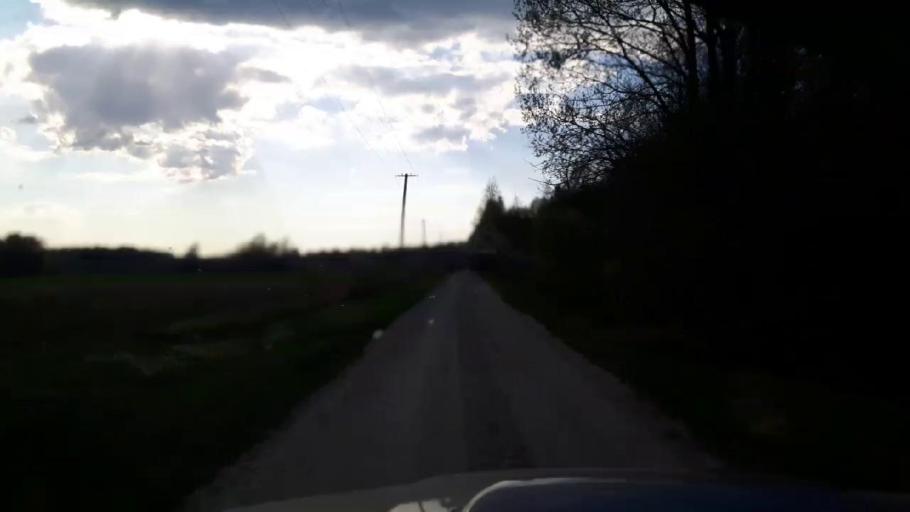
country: EE
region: Paernumaa
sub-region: Tootsi vald
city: Tootsi
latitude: 58.4702
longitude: 24.9092
